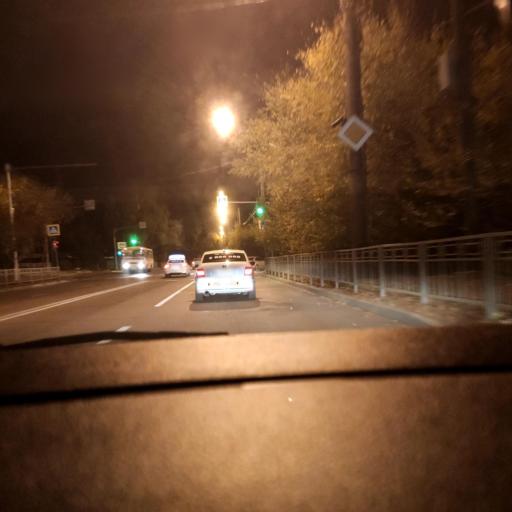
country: RU
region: Voronezj
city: Voronezh
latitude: 51.6940
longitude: 39.1565
